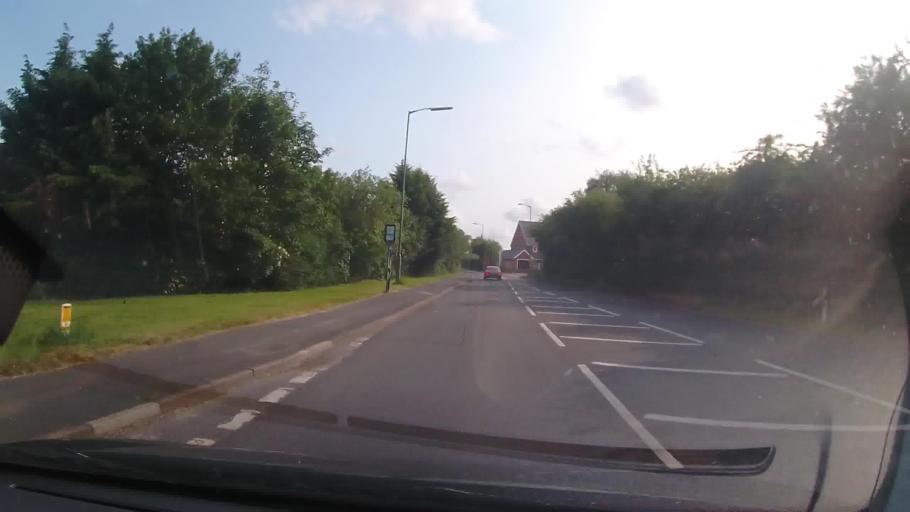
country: GB
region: England
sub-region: Shropshire
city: Shrewsbury
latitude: 52.7297
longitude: -2.7511
